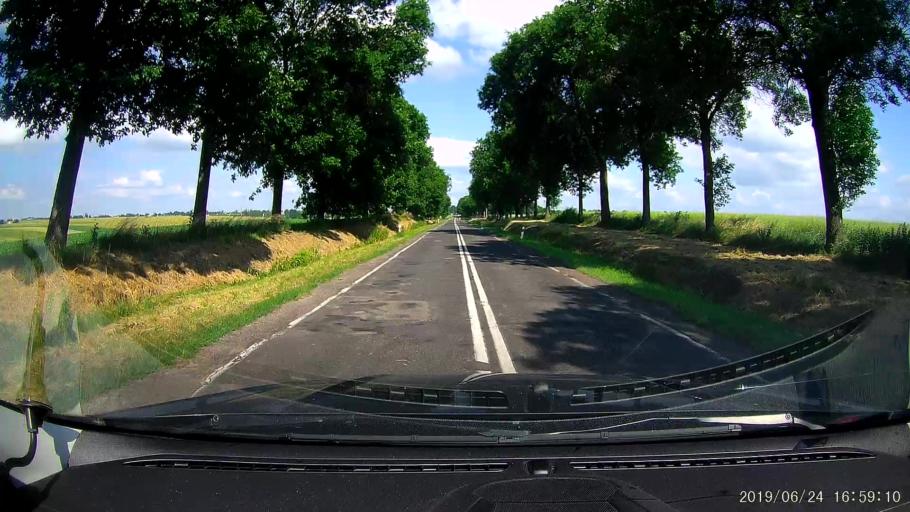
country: PL
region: Lublin Voivodeship
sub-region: Powiat tomaszowski
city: Telatyn
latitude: 50.5240
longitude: 23.8964
